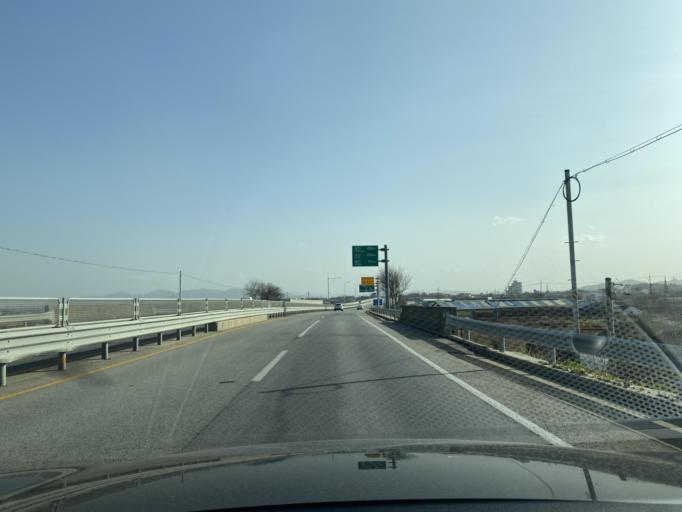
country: KR
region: Chungcheongnam-do
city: Yesan
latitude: 36.6925
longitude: 126.7314
